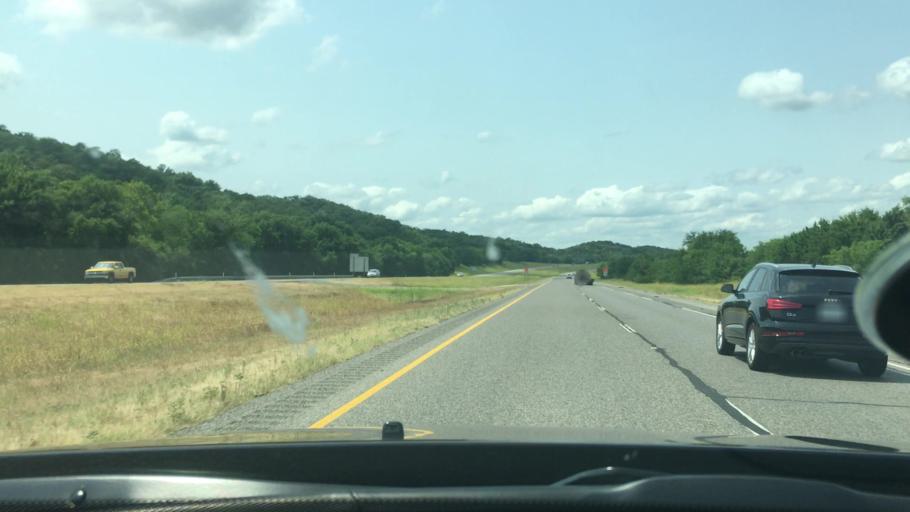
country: US
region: Oklahoma
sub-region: Murray County
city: Davis
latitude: 34.4629
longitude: -97.1468
